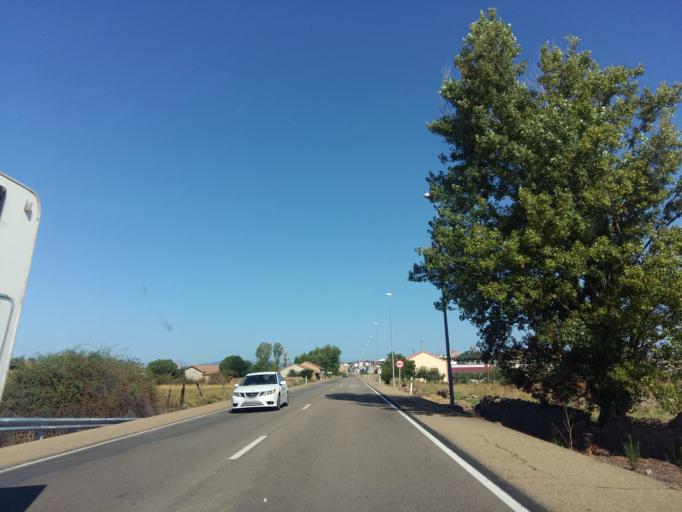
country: ES
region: Castille and Leon
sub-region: Provincia de Leon
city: Astorga
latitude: 42.4450
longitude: -6.0448
